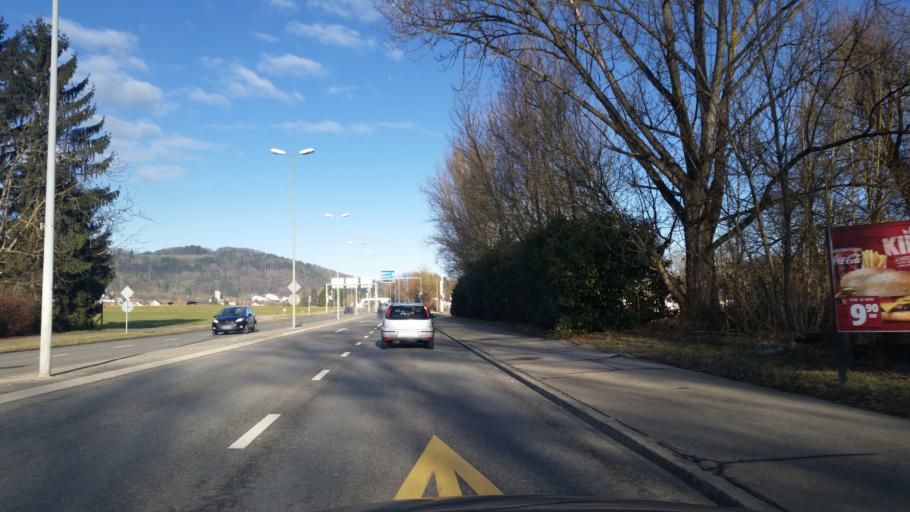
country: CH
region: Zurich
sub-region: Bezirk Dietikon
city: Dietikon / Almend
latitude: 47.4119
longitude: 8.3850
